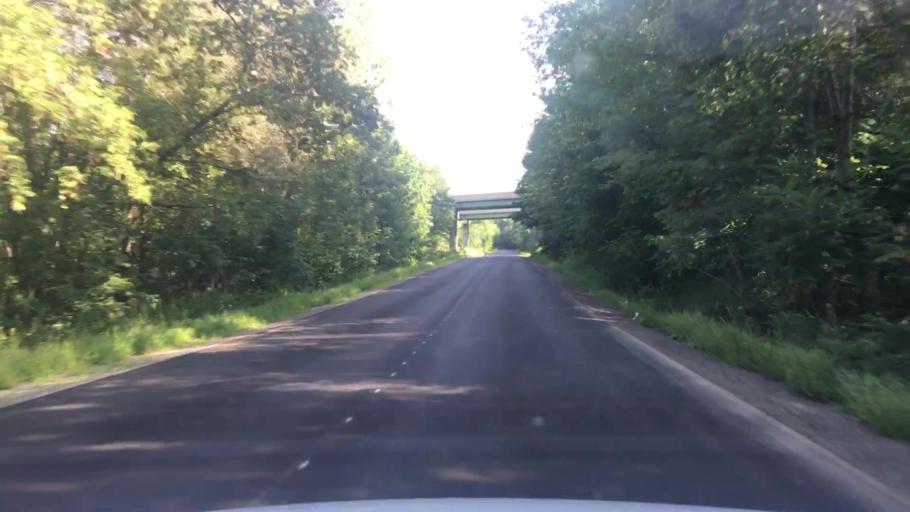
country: US
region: Maine
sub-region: Kennebec County
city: Waterville
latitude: 44.5728
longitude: -69.6571
